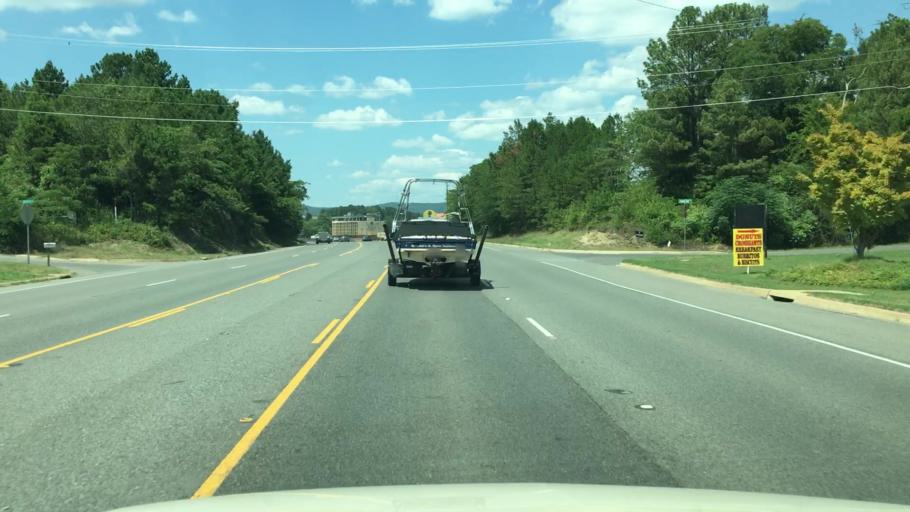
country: US
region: Arkansas
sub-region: Garland County
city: Lake Hamilton
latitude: 34.4367
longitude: -93.0884
